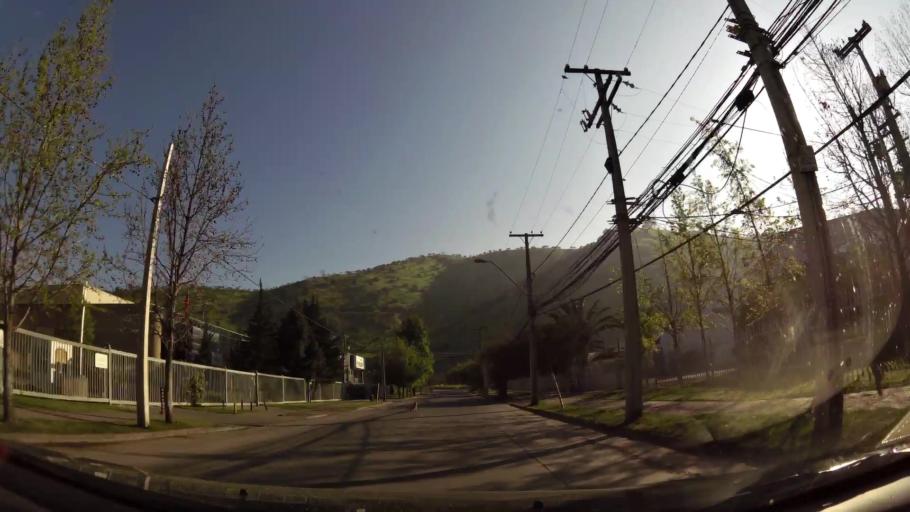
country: CL
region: Santiago Metropolitan
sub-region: Provincia de Santiago
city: Santiago
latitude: -33.3714
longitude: -70.6495
